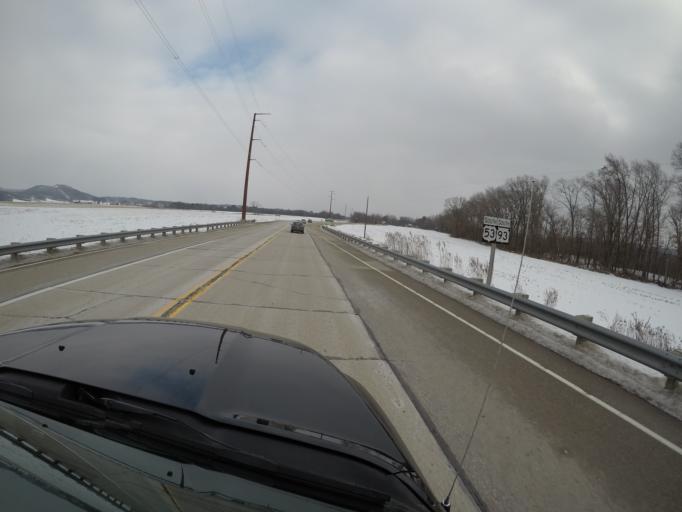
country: US
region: Wisconsin
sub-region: Trempealeau County
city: Galesville
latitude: 44.0719
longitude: -91.3064
